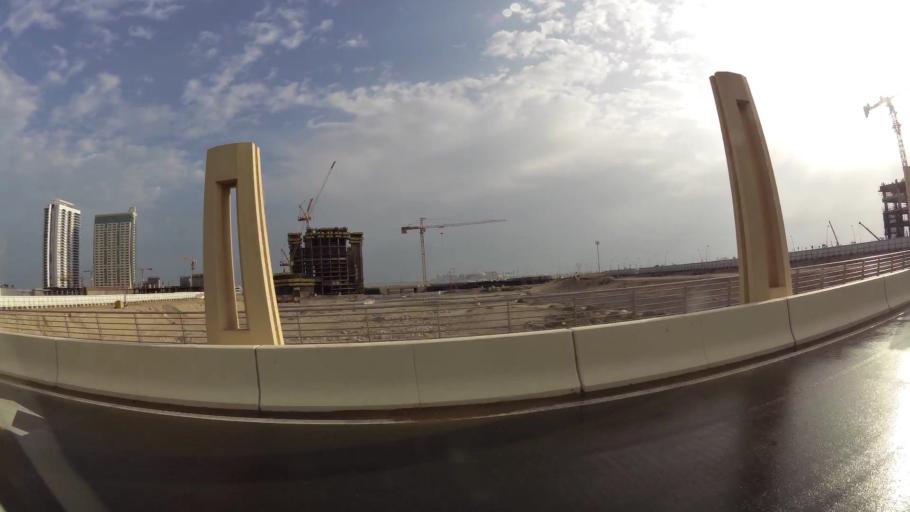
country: AE
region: Abu Dhabi
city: Abu Dhabi
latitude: 24.5049
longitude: 54.4080
